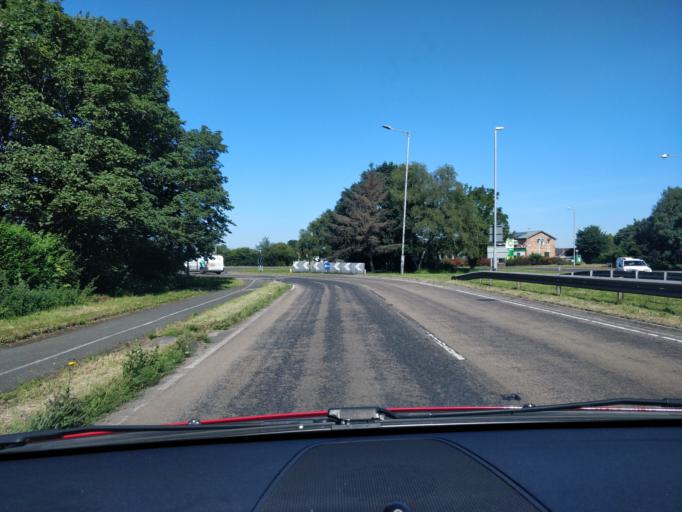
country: GB
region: England
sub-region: Lancashire
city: Banks
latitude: 53.6727
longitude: -2.9212
